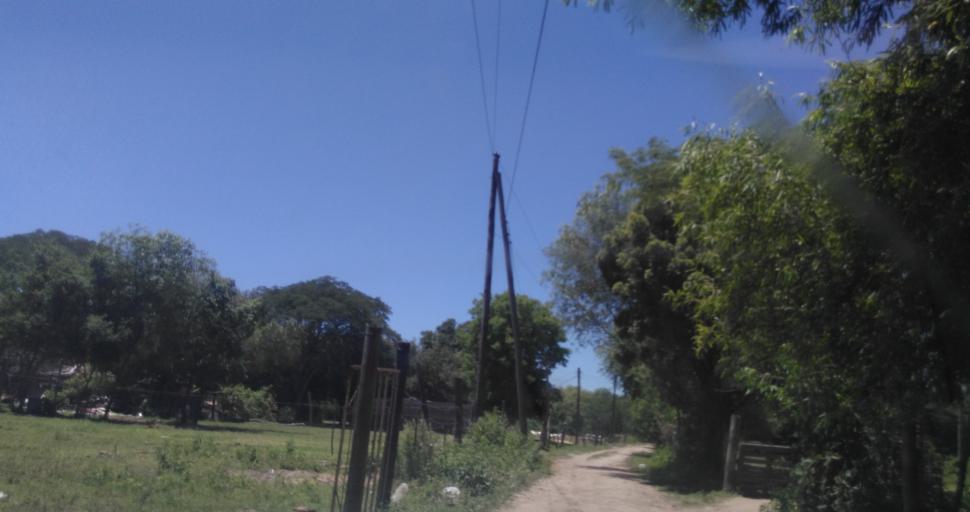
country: AR
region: Chaco
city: Fontana
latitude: -27.4151
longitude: -59.0097
